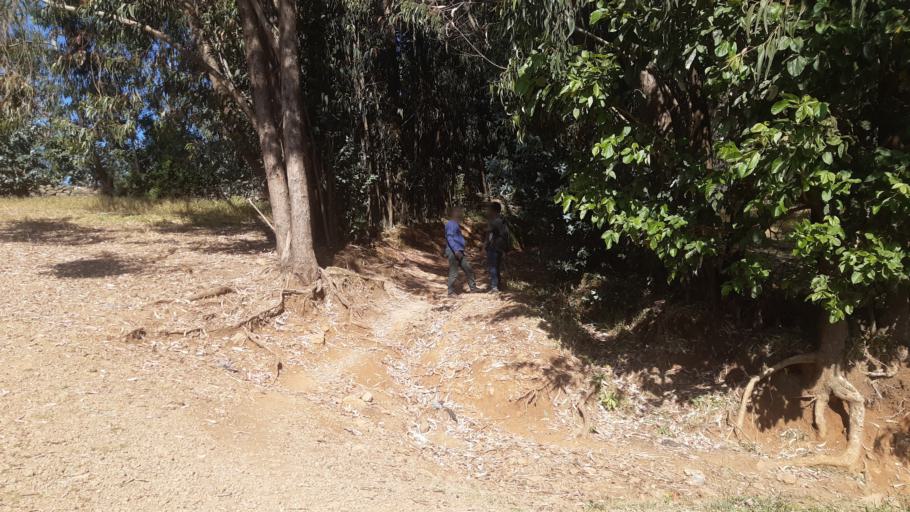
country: ET
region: Amhara
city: Dabat
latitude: 13.3498
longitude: 37.3901
